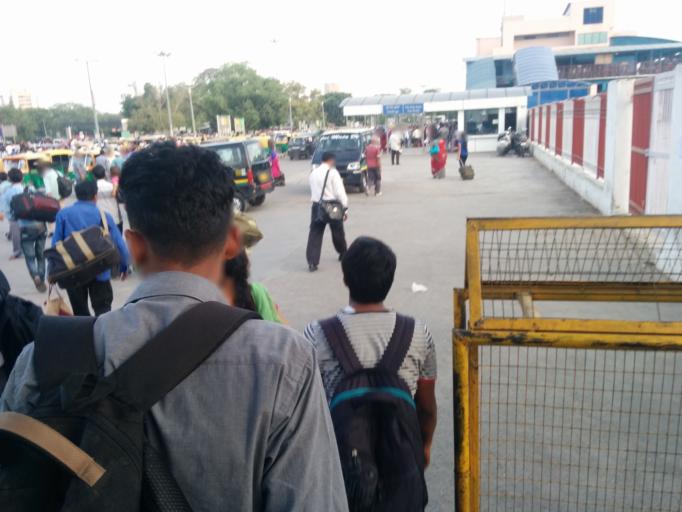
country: IN
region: NCT
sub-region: New Delhi
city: New Delhi
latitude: 28.6434
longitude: 77.2216
